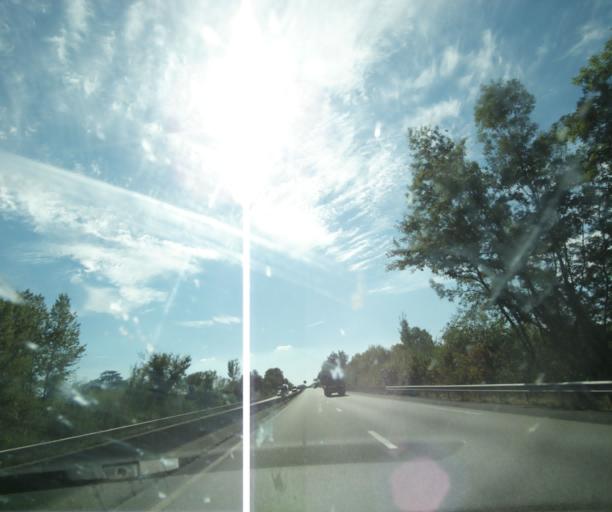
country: FR
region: Limousin
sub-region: Departement de la Correze
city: Ussac
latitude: 45.1701
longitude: 1.4843
